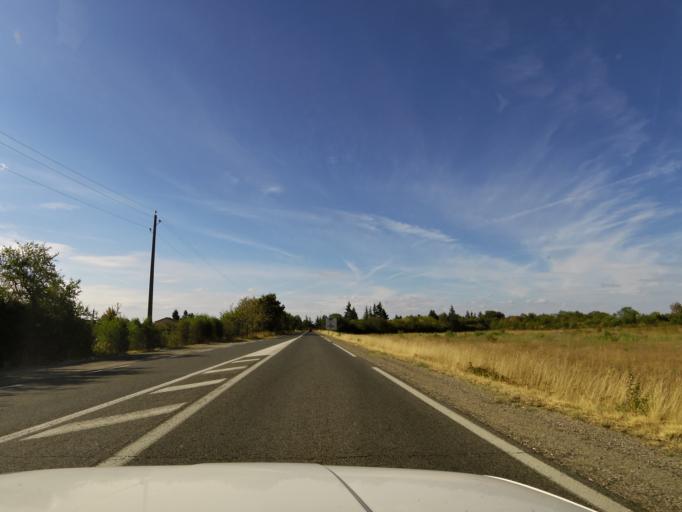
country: FR
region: Rhone-Alpes
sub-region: Departement de l'Ain
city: Saint-Jean-de-Niost
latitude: 45.8476
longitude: 5.2542
